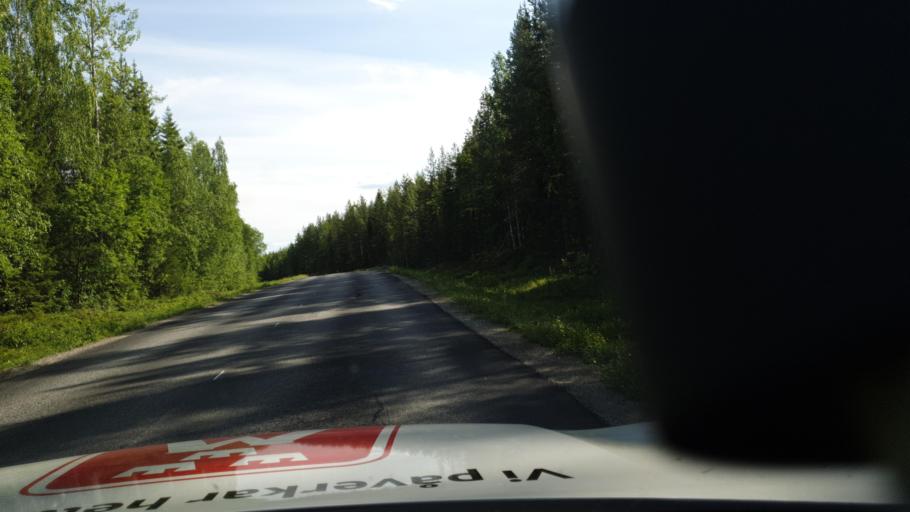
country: SE
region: Vaesterbotten
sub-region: Skelleftea Kommun
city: Boliden
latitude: 64.8392
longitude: 20.3684
